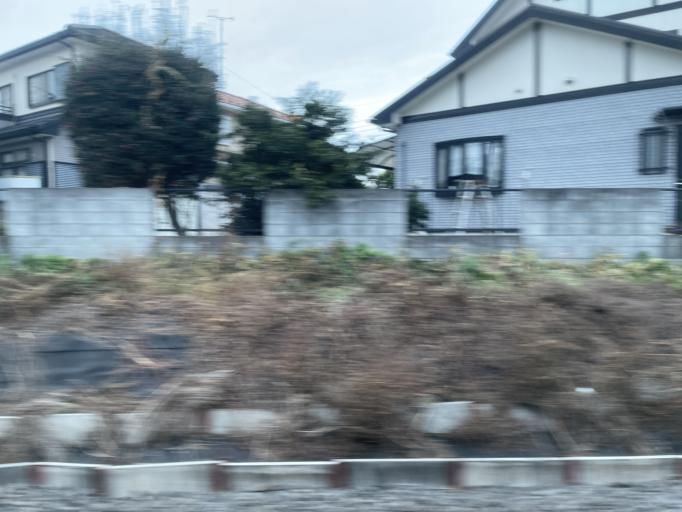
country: JP
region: Saitama
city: Kukichuo
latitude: 36.0710
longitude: 139.6799
